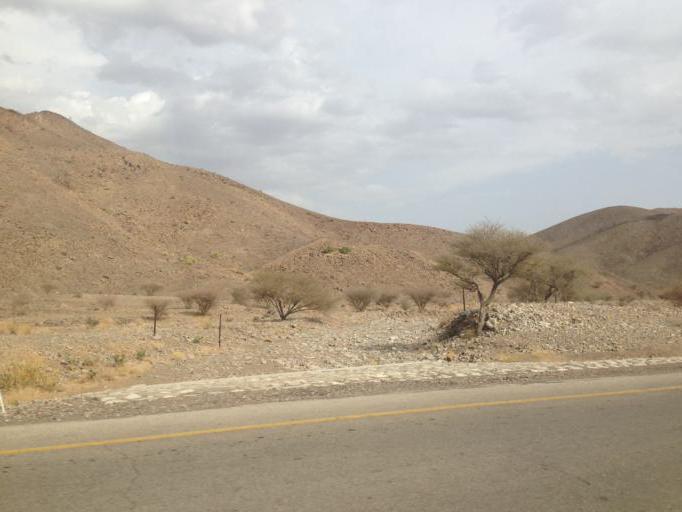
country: OM
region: Ash Sharqiyah
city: Badiyah
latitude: 22.5296
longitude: 58.9553
